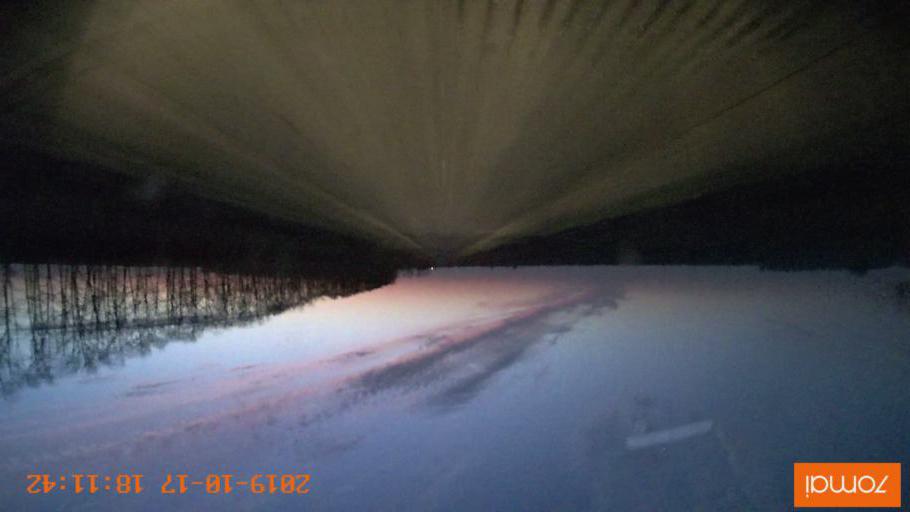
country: RU
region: Tula
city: Kurkino
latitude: 53.4142
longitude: 38.6243
